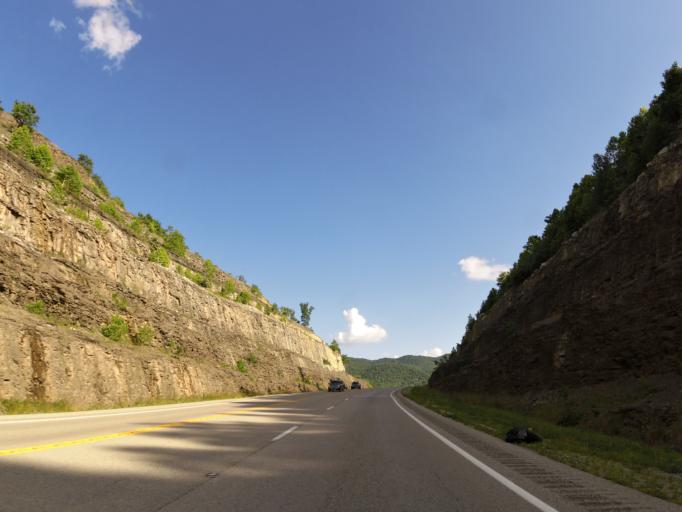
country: US
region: Virginia
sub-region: Lee County
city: Jonesville
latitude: 36.7697
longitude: -83.2028
